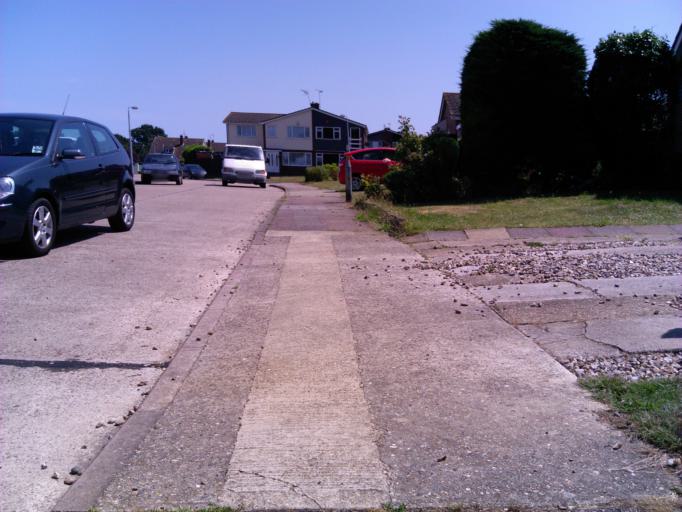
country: GB
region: England
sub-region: Essex
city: Clacton-on-Sea
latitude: 51.8100
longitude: 1.1567
